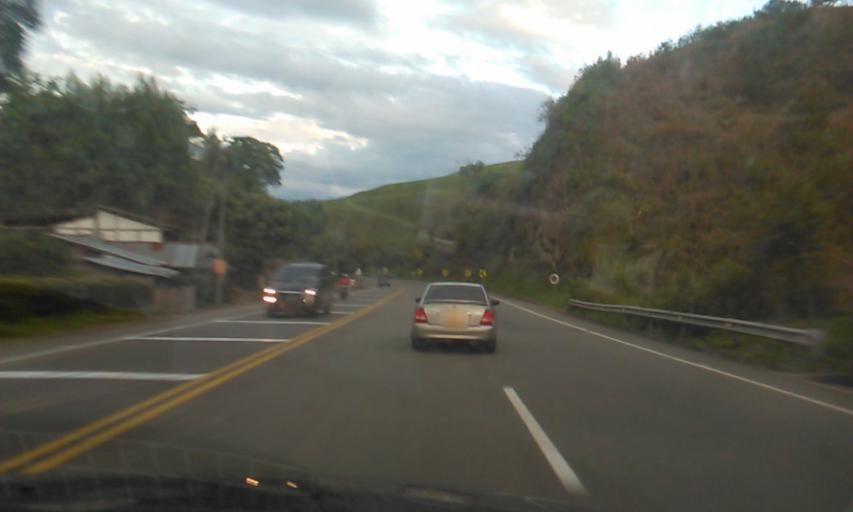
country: CO
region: Valle del Cauca
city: Caicedonia
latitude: 4.4081
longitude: -75.8919
